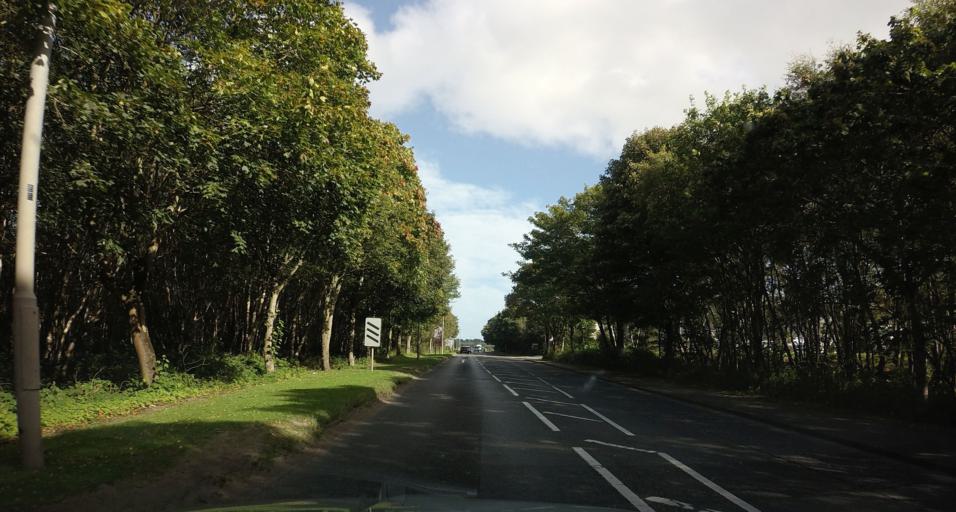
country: GB
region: Scotland
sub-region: Aberdeenshire
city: Westhill
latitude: 57.1502
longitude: -2.2789
